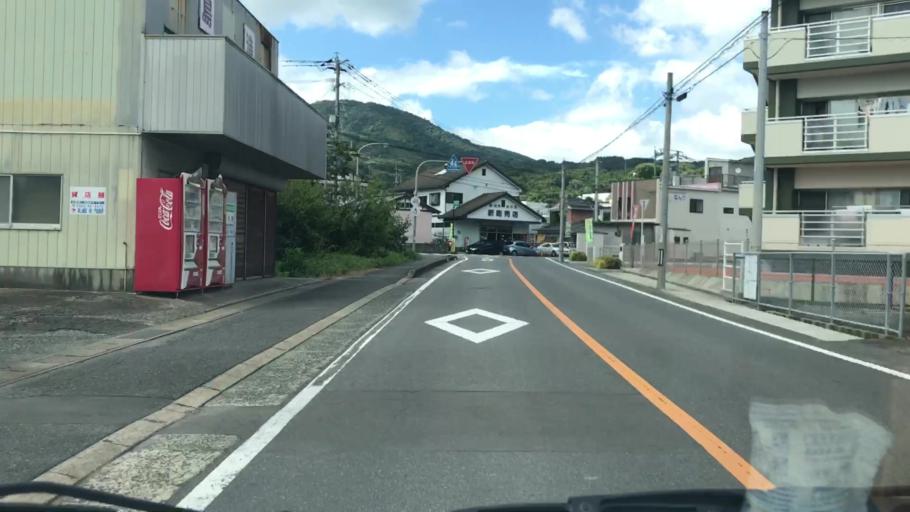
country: JP
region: Saga Prefecture
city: Takeocho-takeo
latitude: 33.2265
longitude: 130.1433
